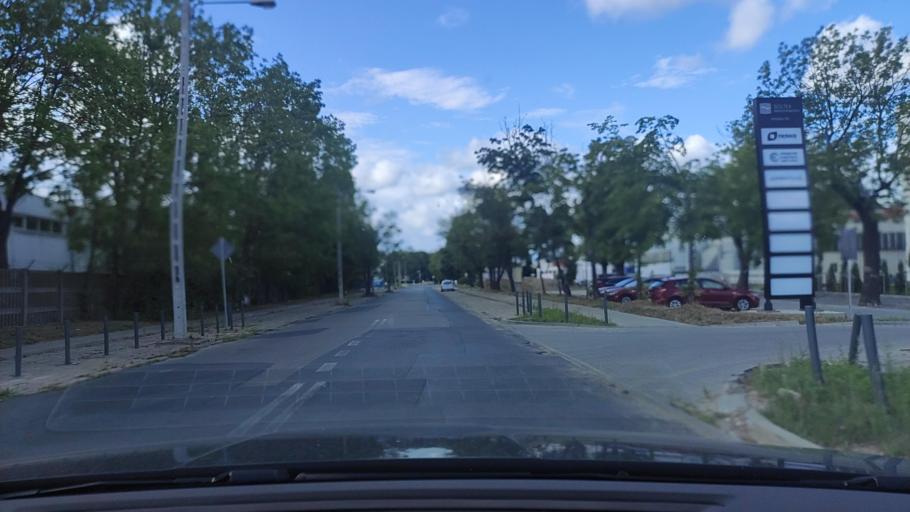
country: PL
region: Greater Poland Voivodeship
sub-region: Poznan
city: Poznan
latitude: 52.4175
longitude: 16.9663
